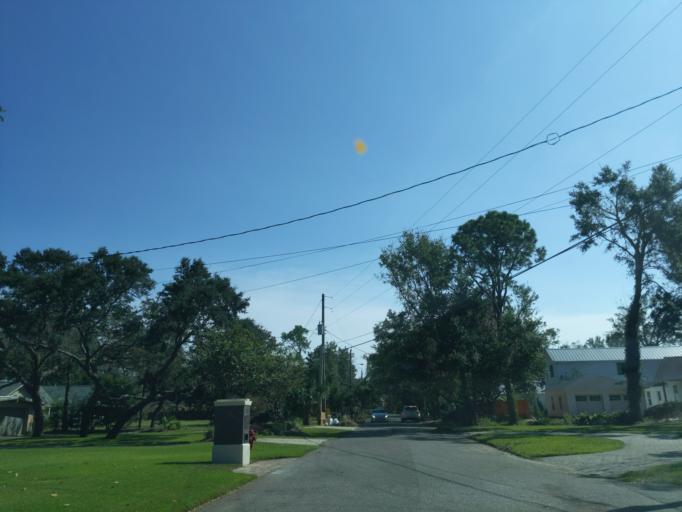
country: US
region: Florida
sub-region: Santa Rosa County
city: Gulf Breeze
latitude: 30.3660
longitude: -87.1832
